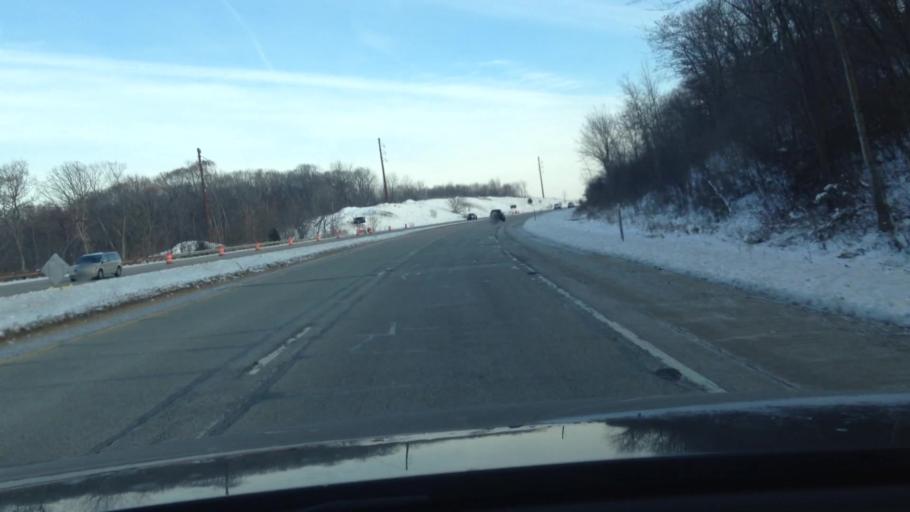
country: US
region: Wisconsin
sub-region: Walworth County
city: Lake Geneva
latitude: 42.6150
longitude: -88.4337
